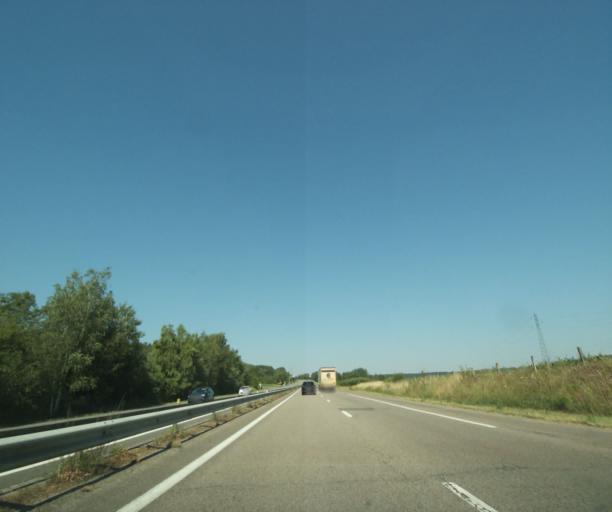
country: FR
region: Lorraine
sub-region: Departement de Meurthe-et-Moselle
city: Domgermain
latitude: 48.6686
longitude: 5.8132
